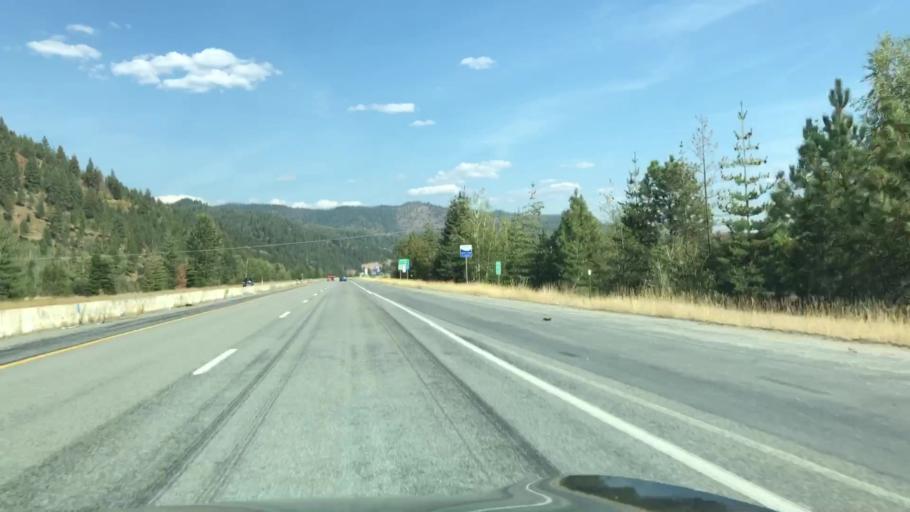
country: US
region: Idaho
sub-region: Shoshone County
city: Kellogg
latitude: 47.5471
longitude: -116.1693
